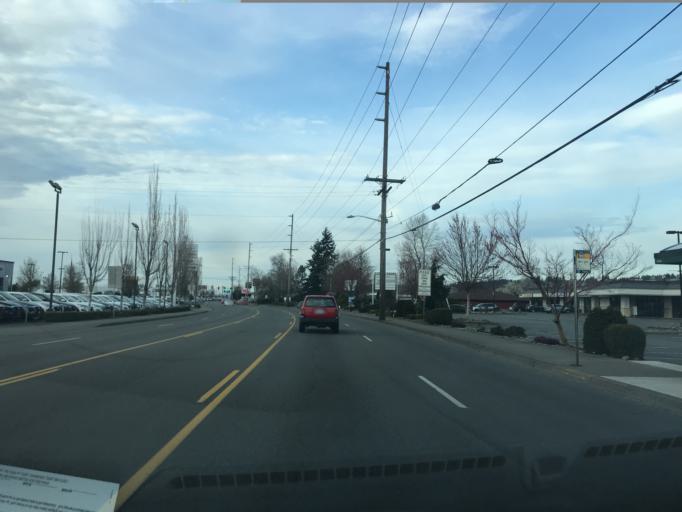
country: US
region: Washington
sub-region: King County
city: Auburn
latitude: 47.3319
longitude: -122.2215
